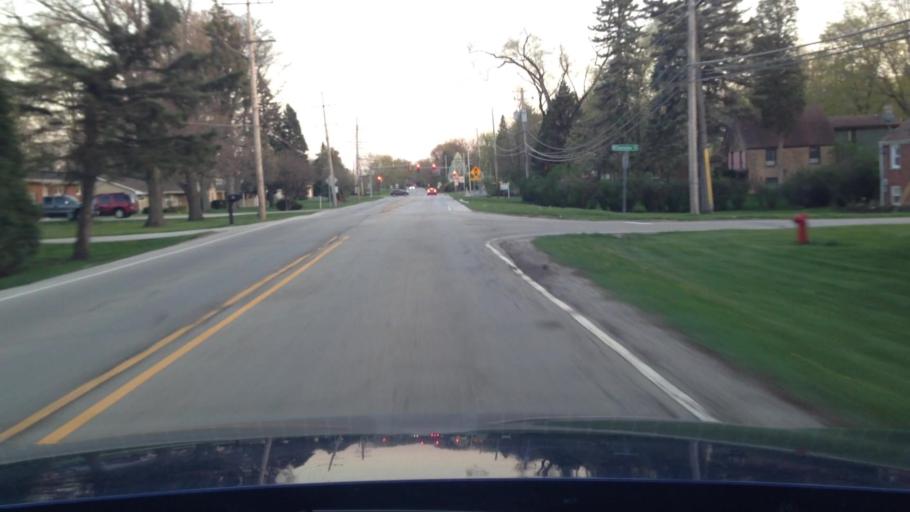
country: US
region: Illinois
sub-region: Cook County
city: Prospect Heights
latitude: 42.0974
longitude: -87.9272
